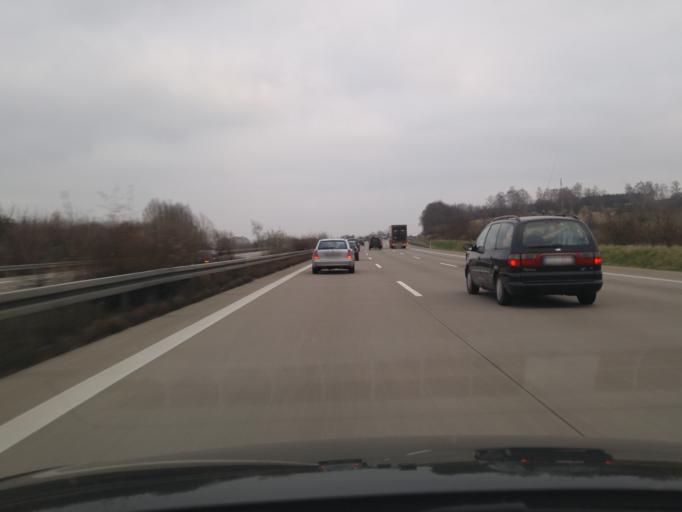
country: DE
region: Saxony-Anhalt
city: Wefensleben
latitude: 52.2085
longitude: 11.1542
